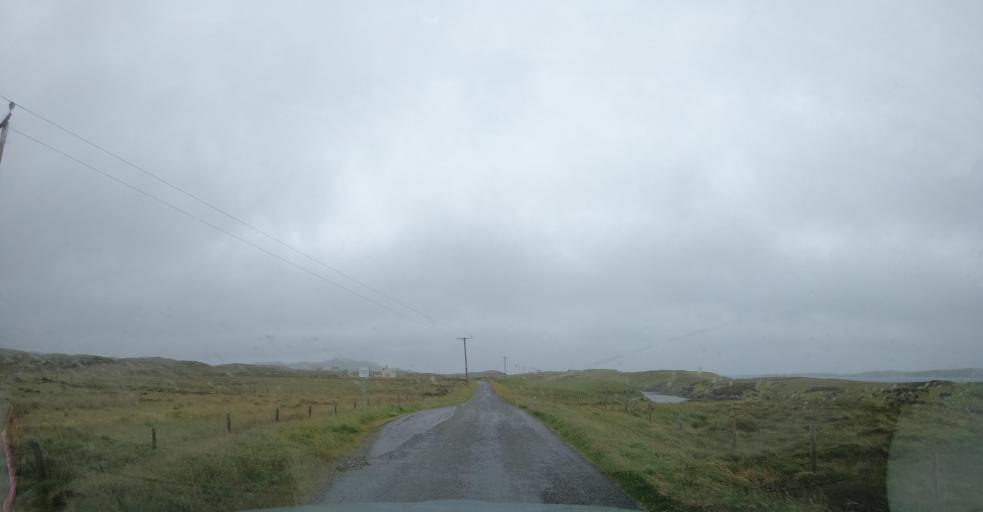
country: GB
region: Scotland
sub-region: Eilean Siar
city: Benbecula
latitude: 57.4793
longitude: -7.2225
